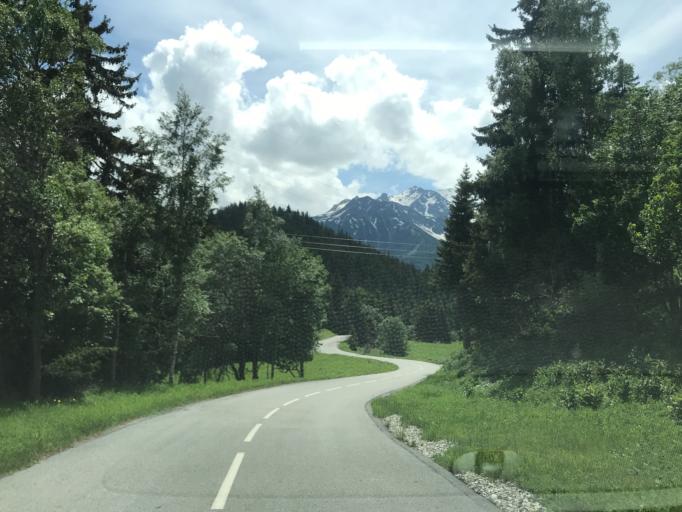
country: FR
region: Rhone-Alpes
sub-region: Departement de la Savoie
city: Modane
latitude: 45.2128
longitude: 6.6484
